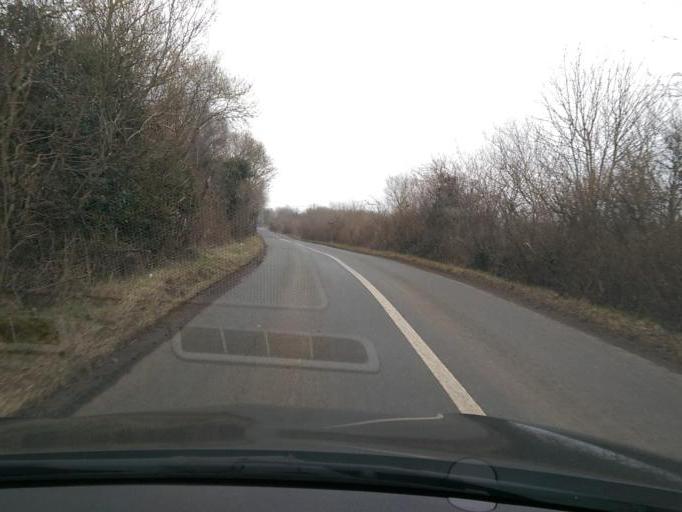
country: IE
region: Leinster
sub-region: An Longfort
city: Lanesborough
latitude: 53.6429
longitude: -7.8770
